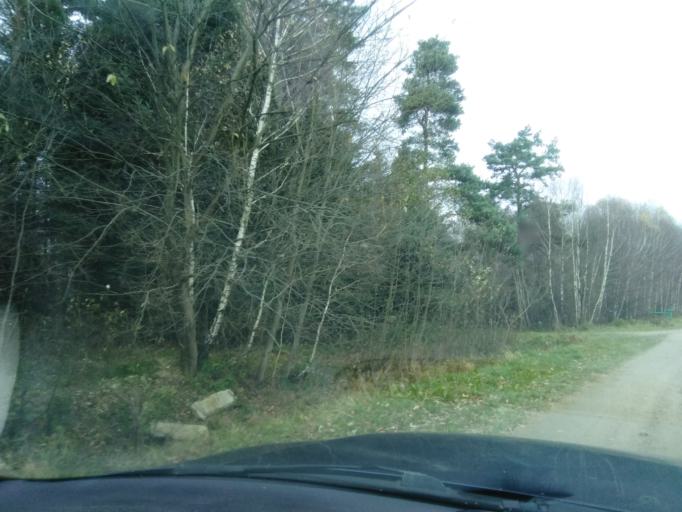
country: PL
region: Subcarpathian Voivodeship
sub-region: Powiat strzyzowski
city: Wysoka Strzyzowska
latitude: 49.7985
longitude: 21.7811
